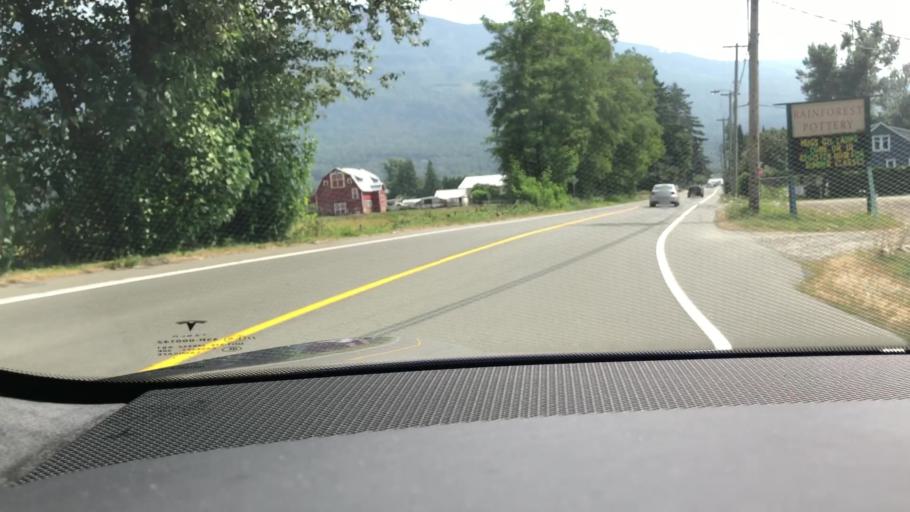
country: CA
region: British Columbia
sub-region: Fraser Valley Regional District
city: Chilliwack
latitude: 49.0880
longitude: -122.0649
